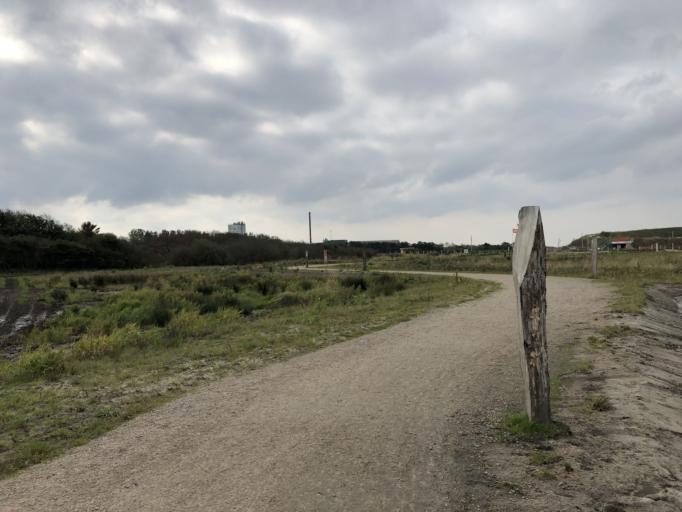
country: DK
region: Central Jutland
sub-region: Ringkobing-Skjern Kommune
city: Ringkobing
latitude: 56.1018
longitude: 8.2466
